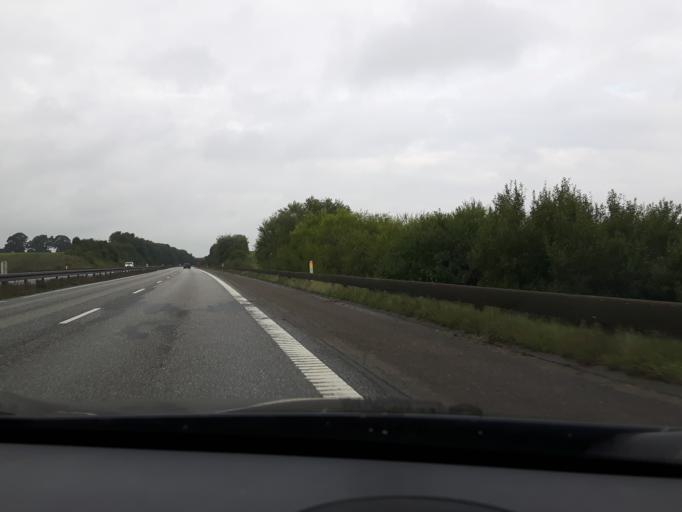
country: DK
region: North Denmark
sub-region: Mariagerfjord Kommune
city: Hobro
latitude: 56.6011
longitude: 9.7547
